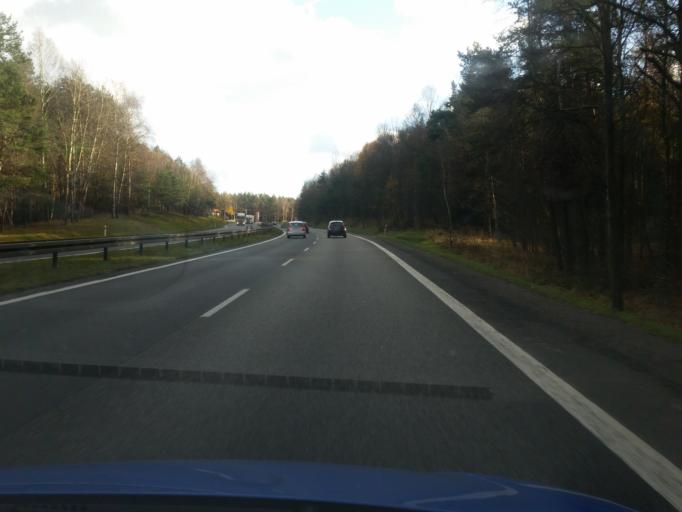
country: PL
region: Silesian Voivodeship
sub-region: Powiat czestochowski
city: Kamienica Polska
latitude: 50.6643
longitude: 19.1251
